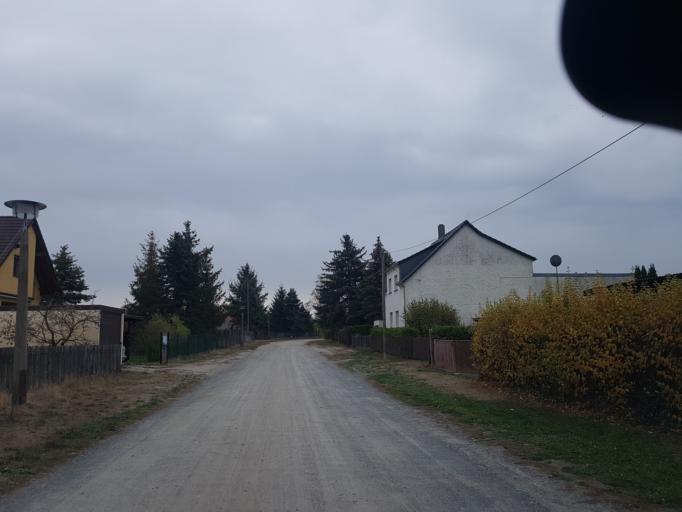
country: DE
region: Brandenburg
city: Finsterwalde
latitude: 51.6141
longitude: 13.7211
